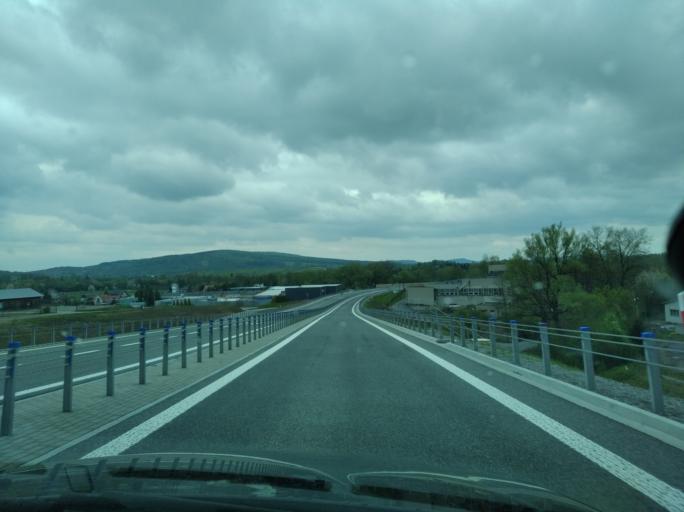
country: PL
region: Subcarpathian Voivodeship
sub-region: Powiat sanocki
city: Sanok
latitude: 49.5625
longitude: 22.1580
